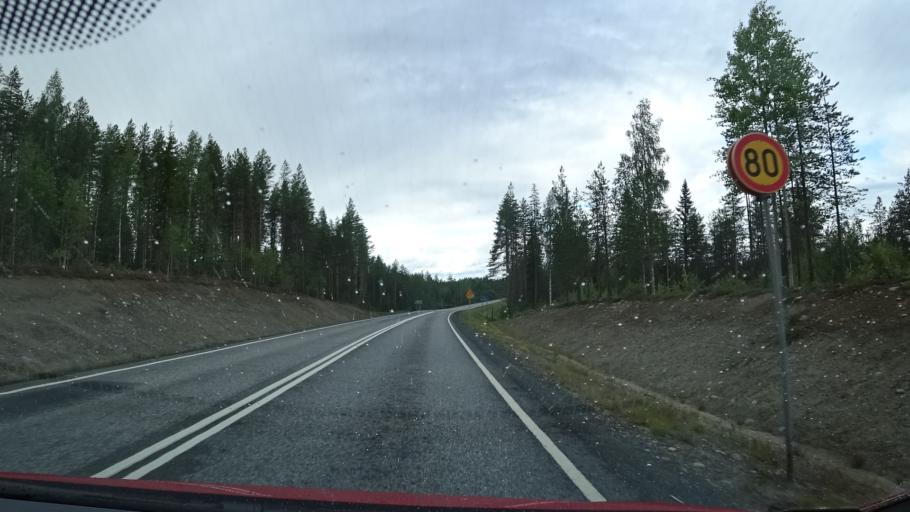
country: FI
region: Kainuu
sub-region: Kehys-Kainuu
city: Kuhmo
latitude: 64.0764
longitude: 29.4902
